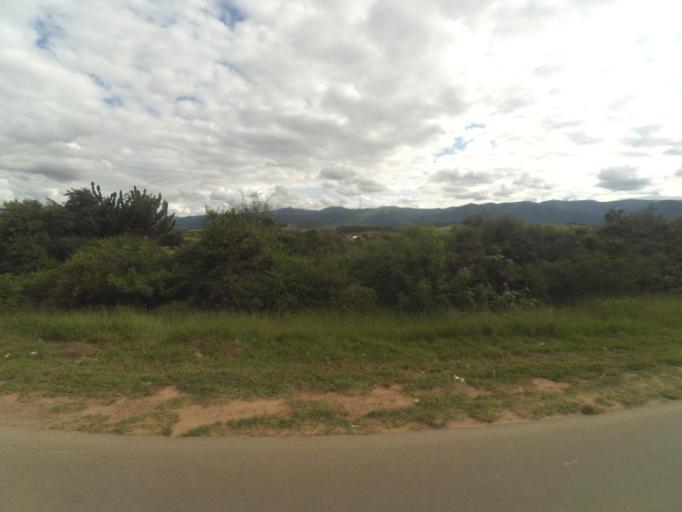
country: BO
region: Santa Cruz
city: Samaipata
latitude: -18.1603
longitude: -63.9162
